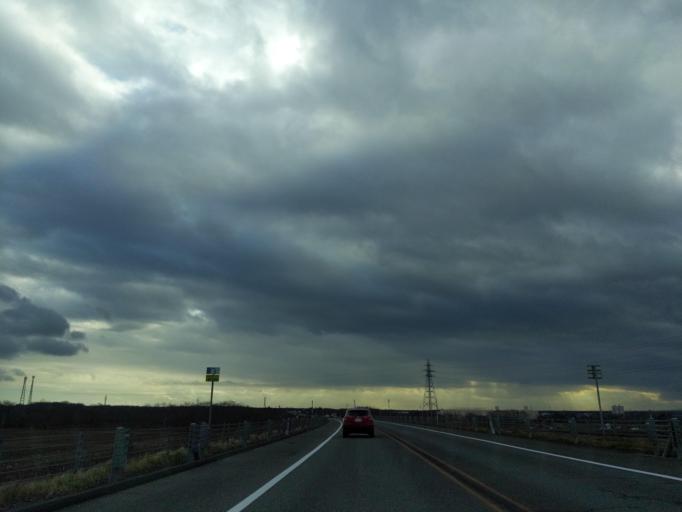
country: JP
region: Hokkaido
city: Chitose
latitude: 42.8406
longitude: 141.6936
